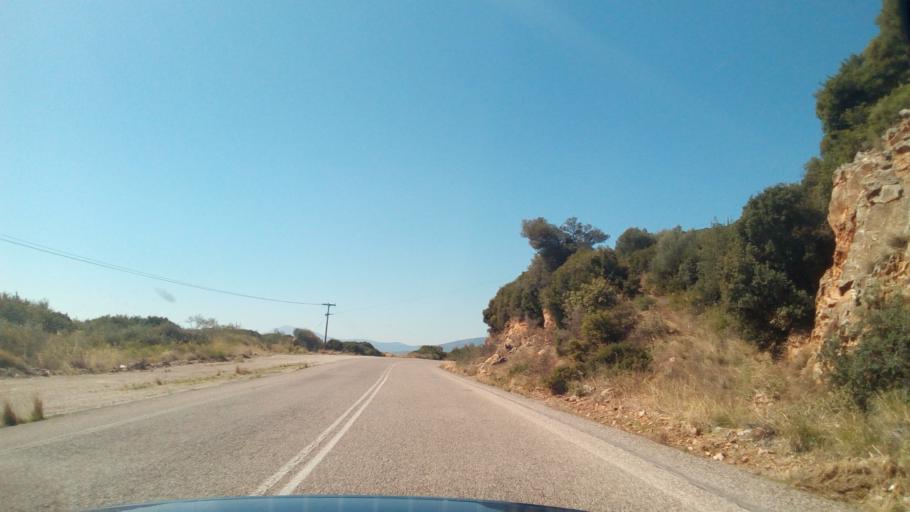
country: GR
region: West Greece
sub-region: Nomos Achaias
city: Kamarai
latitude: 38.4057
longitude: 21.9644
